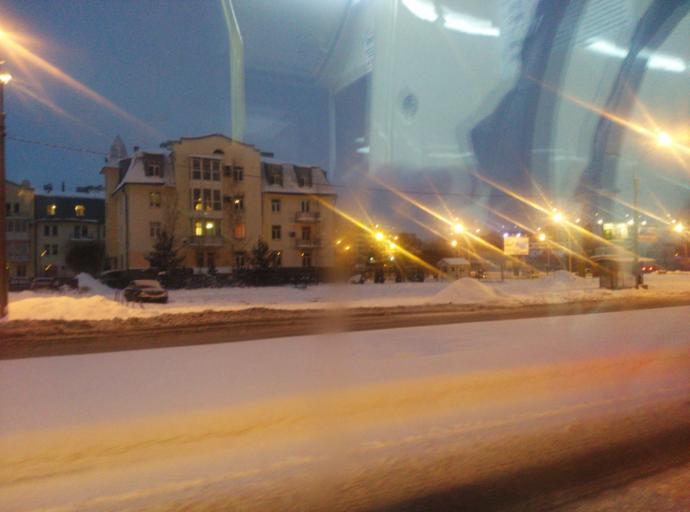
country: RU
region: St.-Petersburg
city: Kolomyagi
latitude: 60.0176
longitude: 30.2768
